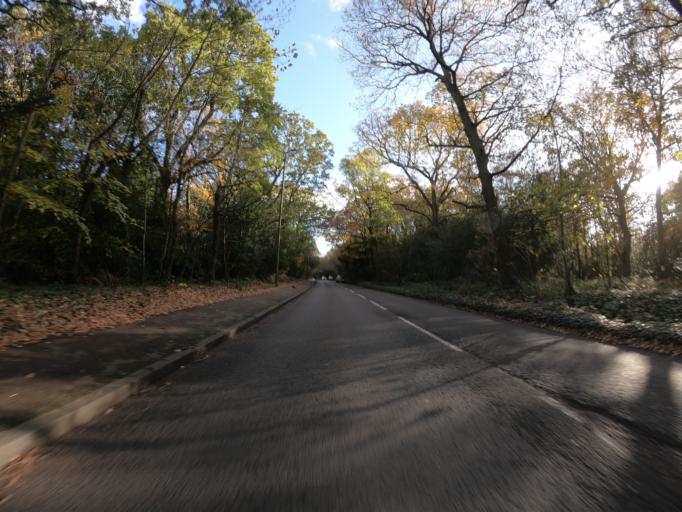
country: GB
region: England
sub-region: Greater London
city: Chislehurst
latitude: 51.4156
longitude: 0.0702
